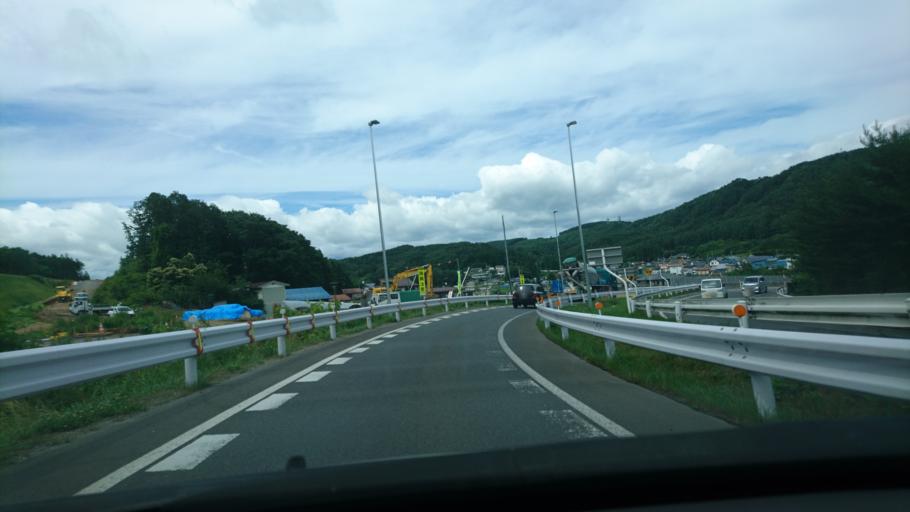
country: JP
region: Aomori
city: Hachinohe
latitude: 40.2210
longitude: 141.7826
